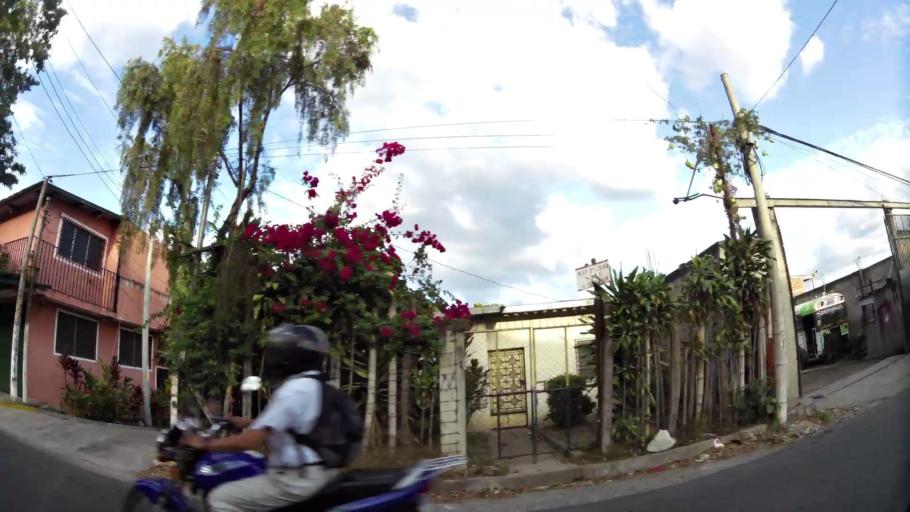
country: SV
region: Cuscatlan
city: Cojutepeque
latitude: 13.7165
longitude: -88.9269
